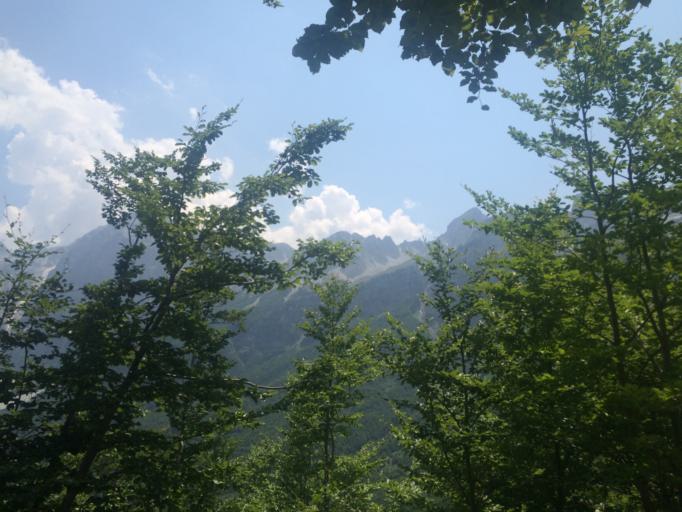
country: AL
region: Kukes
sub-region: Rrethi i Tropojes
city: Valbone
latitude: 42.4123
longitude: 19.8276
